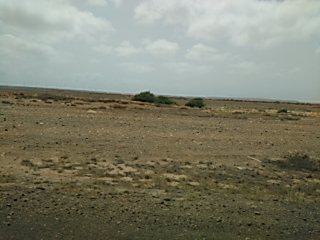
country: CV
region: Sal
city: Espargos
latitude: 16.7040
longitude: -22.9398
